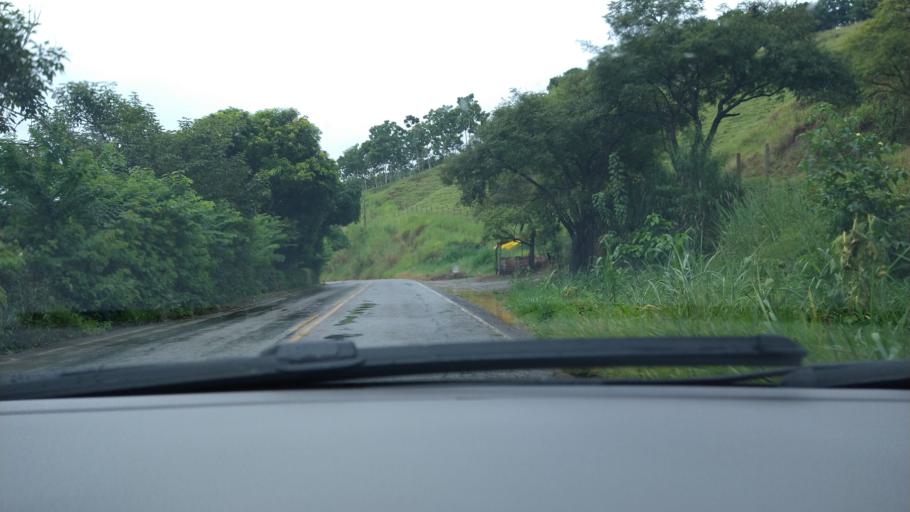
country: BR
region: Minas Gerais
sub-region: Ponte Nova
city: Ponte Nova
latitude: -20.3761
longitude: -42.8974
